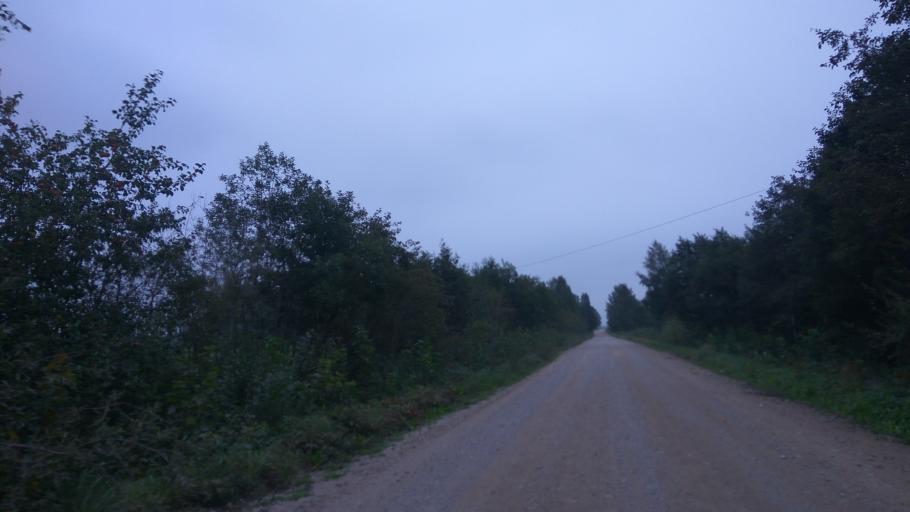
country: LV
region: Rucavas
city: Rucava
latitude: 56.1654
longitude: 21.1716
